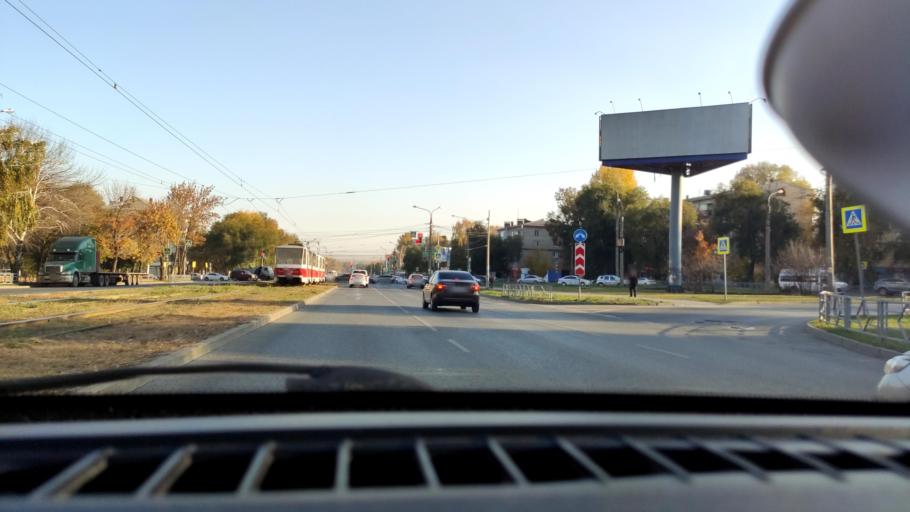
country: RU
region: Samara
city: Samara
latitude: 53.2134
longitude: 50.2265
